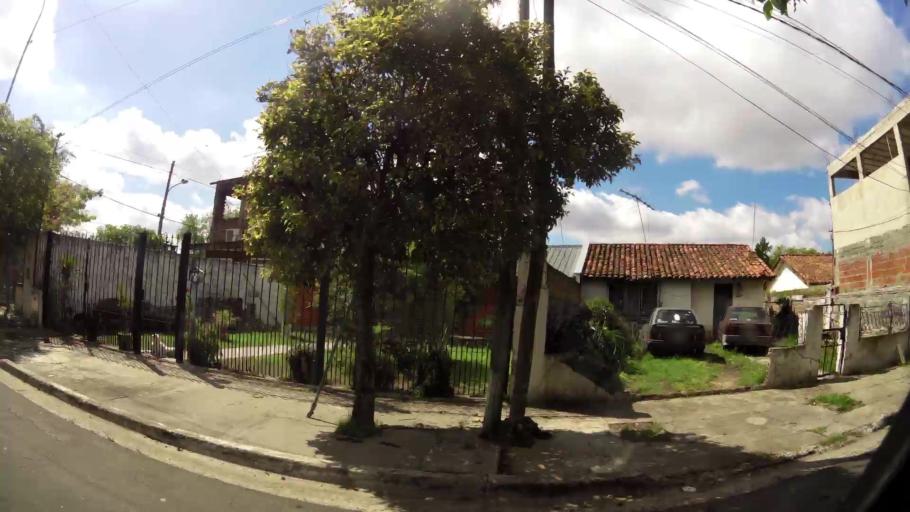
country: AR
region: Buenos Aires
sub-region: Partido de Lanus
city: Lanus
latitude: -34.6722
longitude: -58.4189
